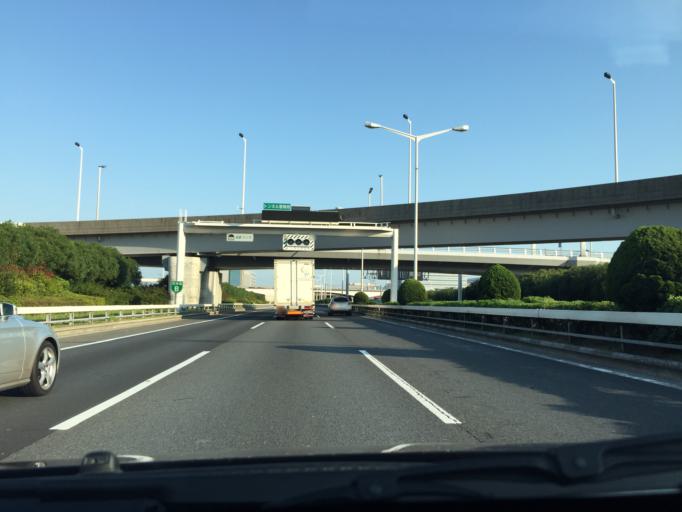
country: JP
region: Kanagawa
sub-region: Kawasaki-shi
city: Kawasaki
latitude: 35.5478
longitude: 139.7880
